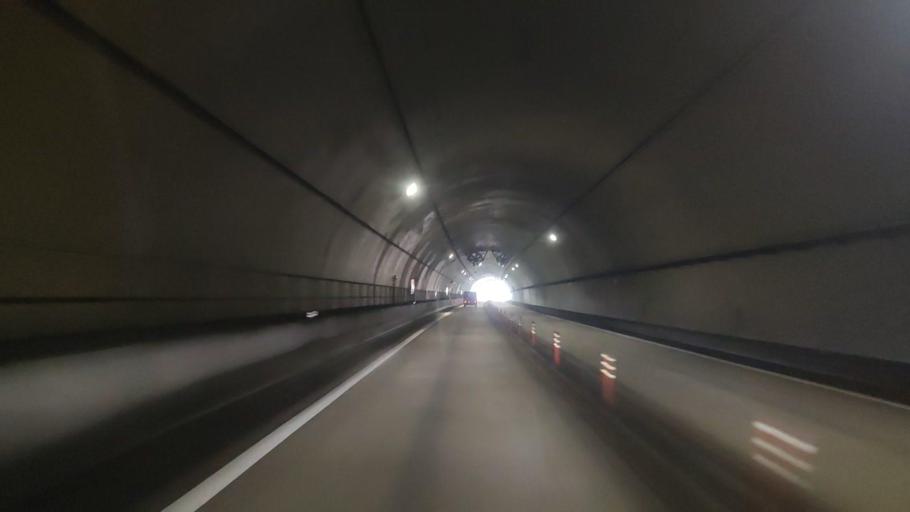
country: JP
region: Wakayama
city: Tanabe
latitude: 33.5517
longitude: 135.5135
